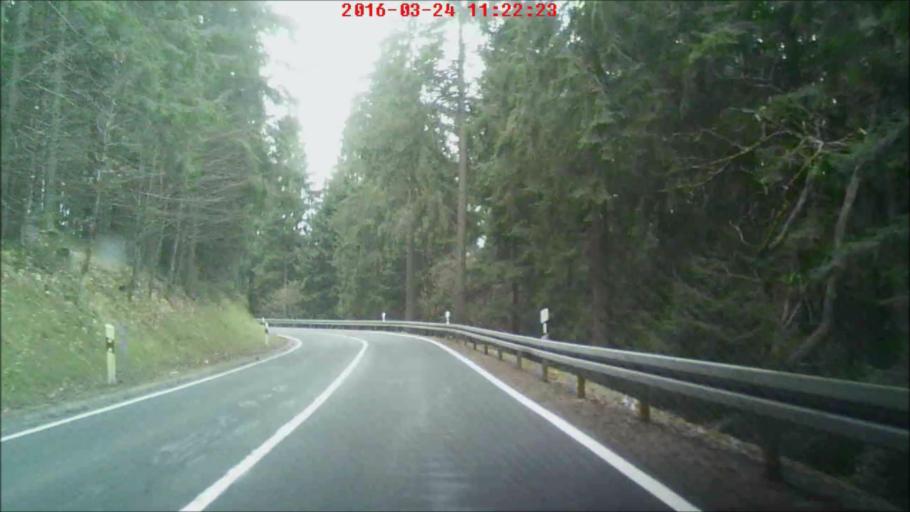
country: DE
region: Thuringia
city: Eisfeld
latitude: 50.4860
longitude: 10.9217
